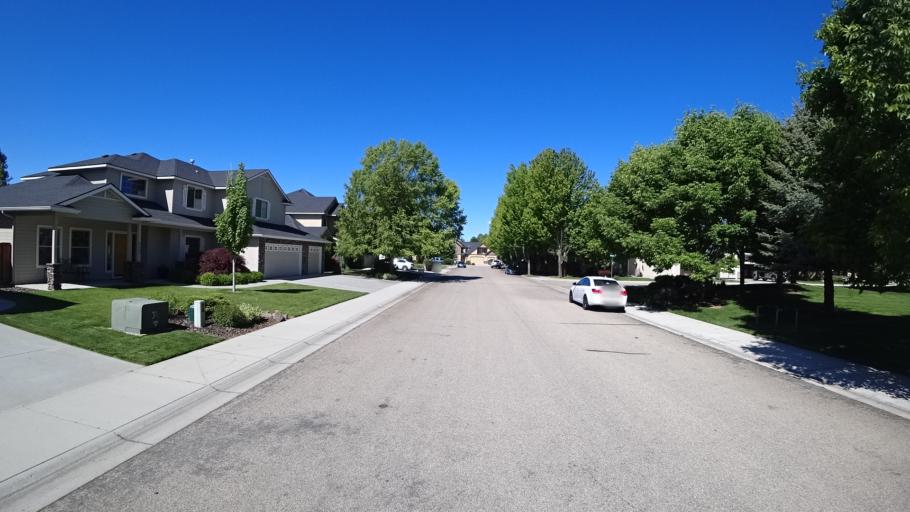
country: US
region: Idaho
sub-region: Ada County
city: Meridian
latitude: 43.6379
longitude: -116.3651
